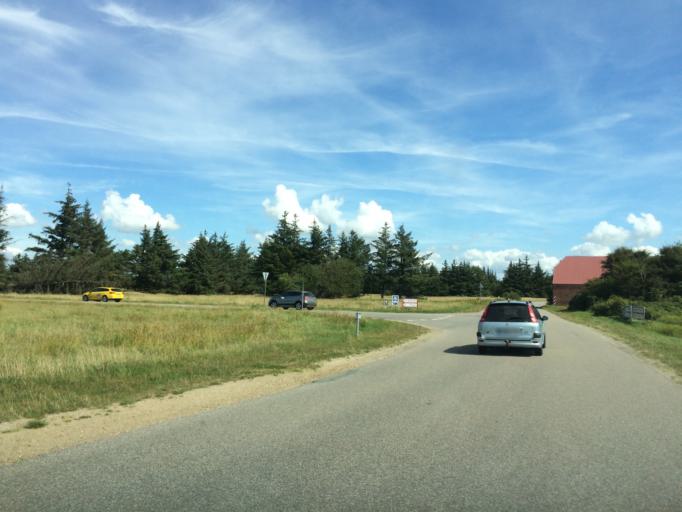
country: DK
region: South Denmark
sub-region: Varde Kommune
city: Oksbol
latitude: 55.6658
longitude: 8.1933
